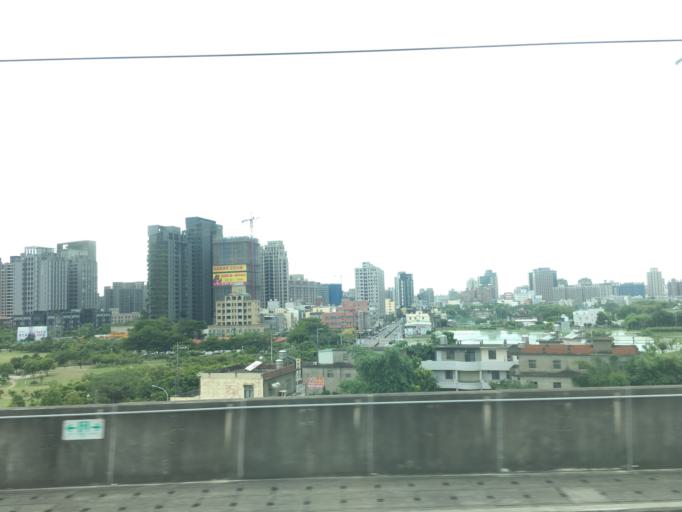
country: TW
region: Taiwan
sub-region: Hsinchu
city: Zhubei
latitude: 24.8128
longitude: 121.0413
